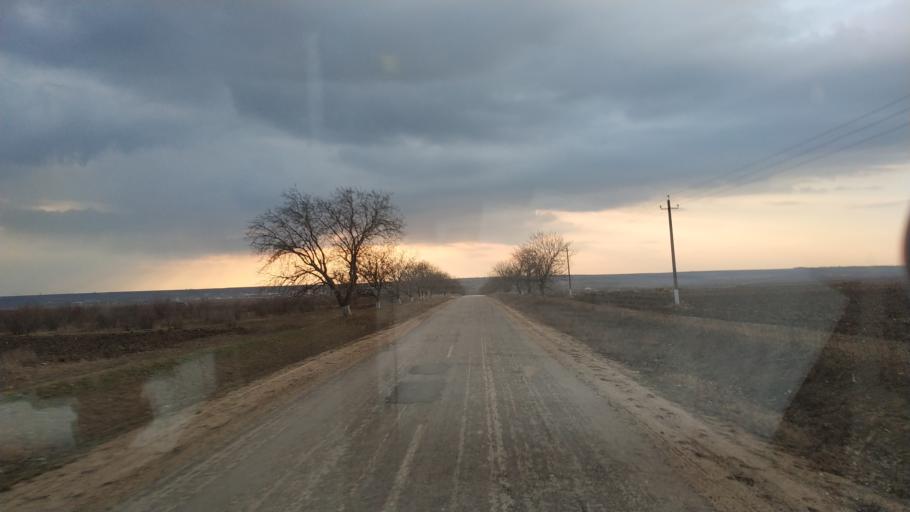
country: MD
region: Telenesti
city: Grigoriopol
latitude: 47.0242
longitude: 29.3274
